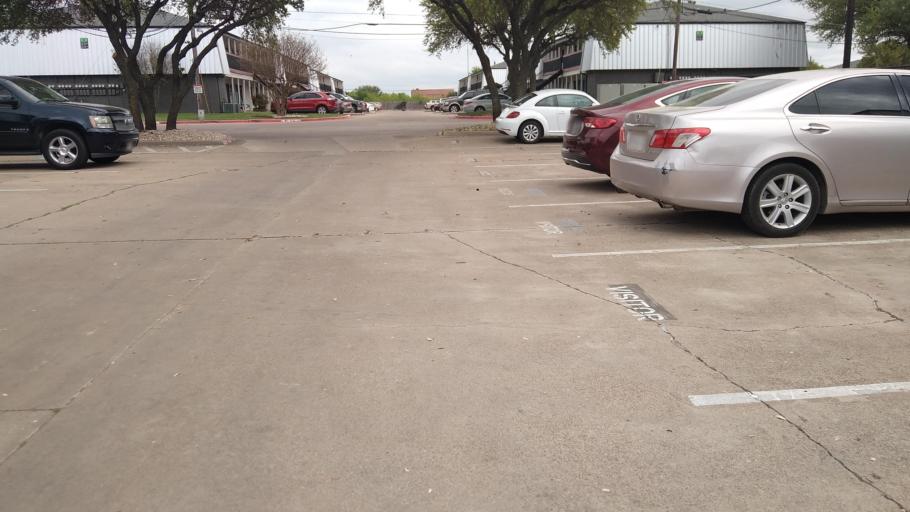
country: US
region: Texas
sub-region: McLennan County
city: Beverly
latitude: 31.5249
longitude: -97.1240
